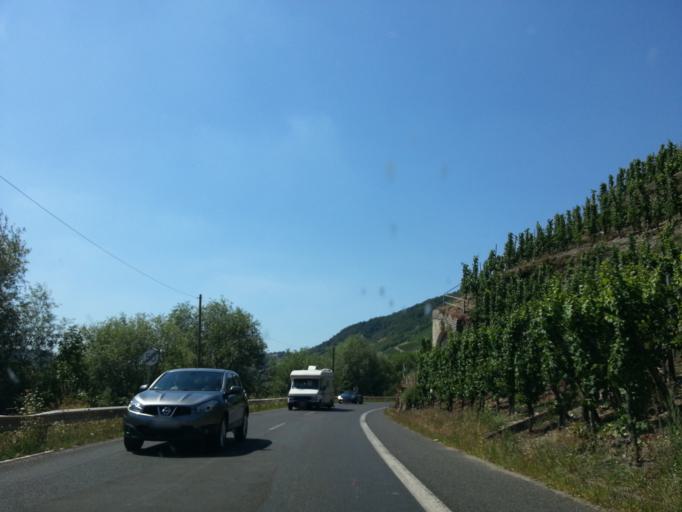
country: DE
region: Rheinland-Pfalz
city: Kesten
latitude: 49.8987
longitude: 6.9536
